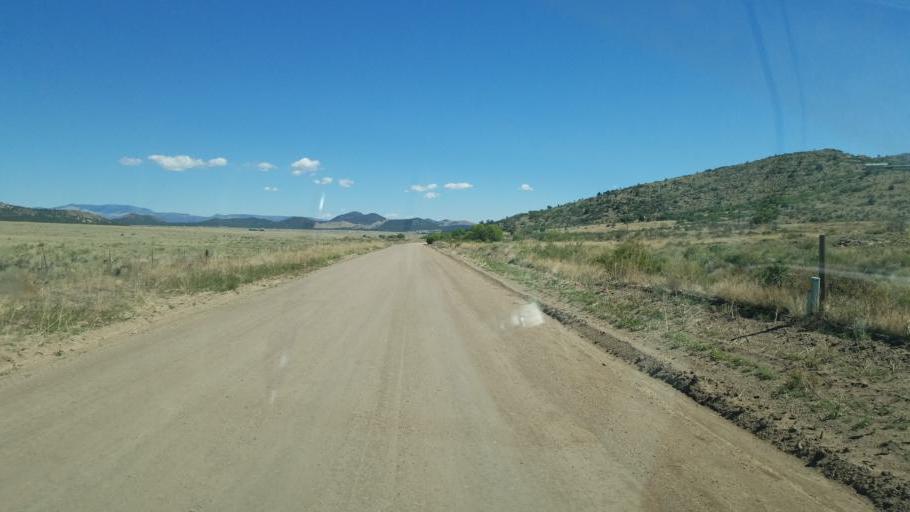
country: US
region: Colorado
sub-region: Custer County
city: Westcliffe
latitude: 38.2374
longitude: -105.5022
